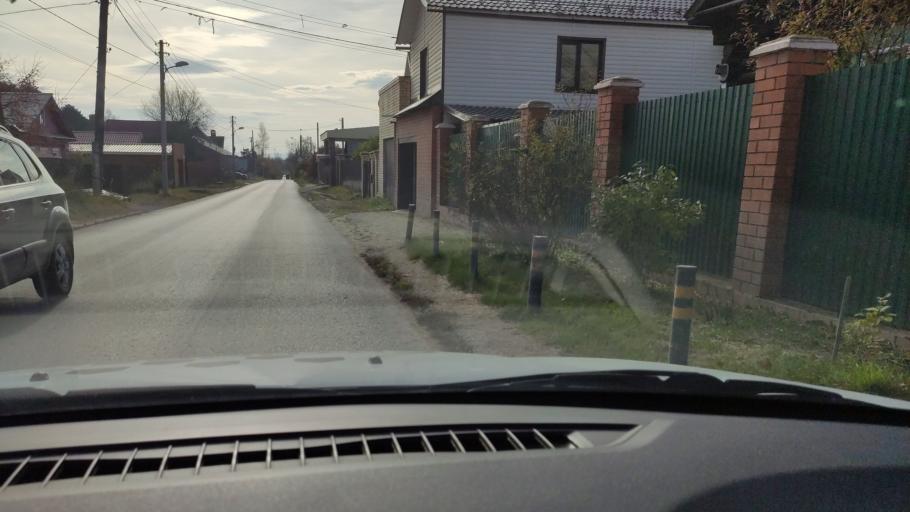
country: RU
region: Perm
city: Kondratovo
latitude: 58.0465
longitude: 56.1199
